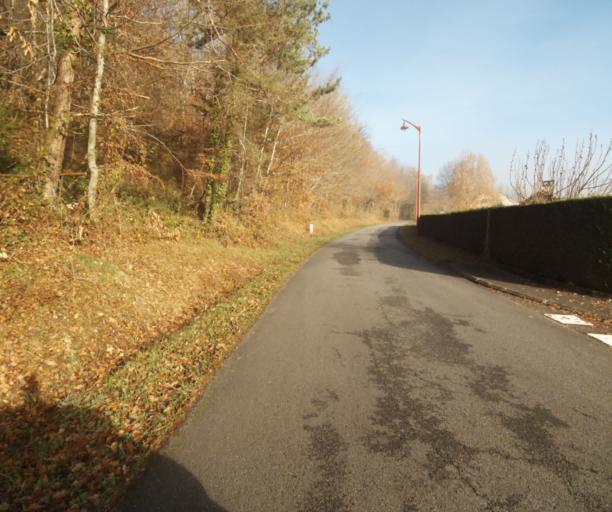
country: FR
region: Limousin
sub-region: Departement de la Correze
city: Laguenne
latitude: 45.2510
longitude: 1.7830
